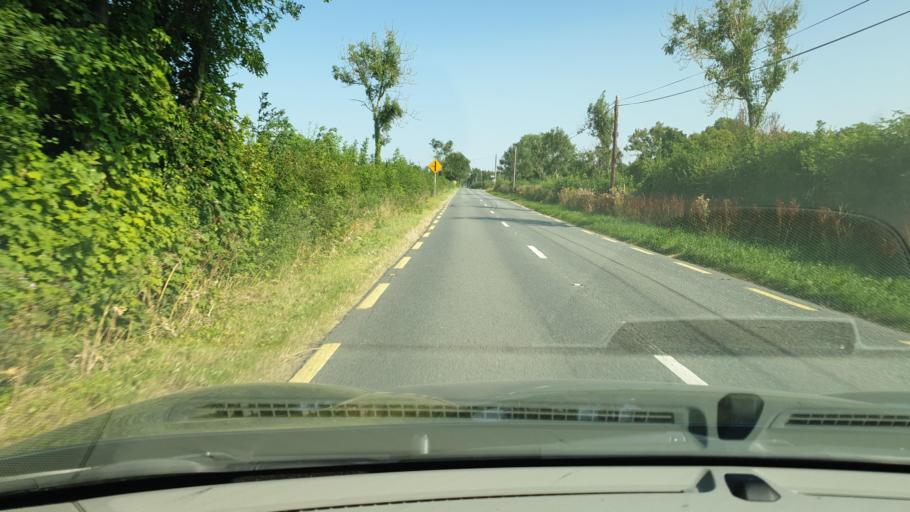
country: IE
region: Leinster
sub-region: An Mhi
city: Athboy
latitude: 53.6443
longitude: -6.8509
